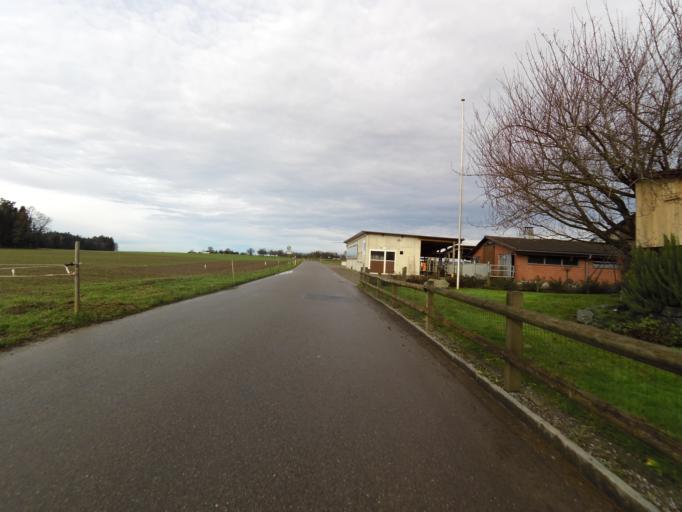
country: CH
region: Thurgau
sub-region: Frauenfeld District
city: Thundorf
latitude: 47.5571
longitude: 8.9357
